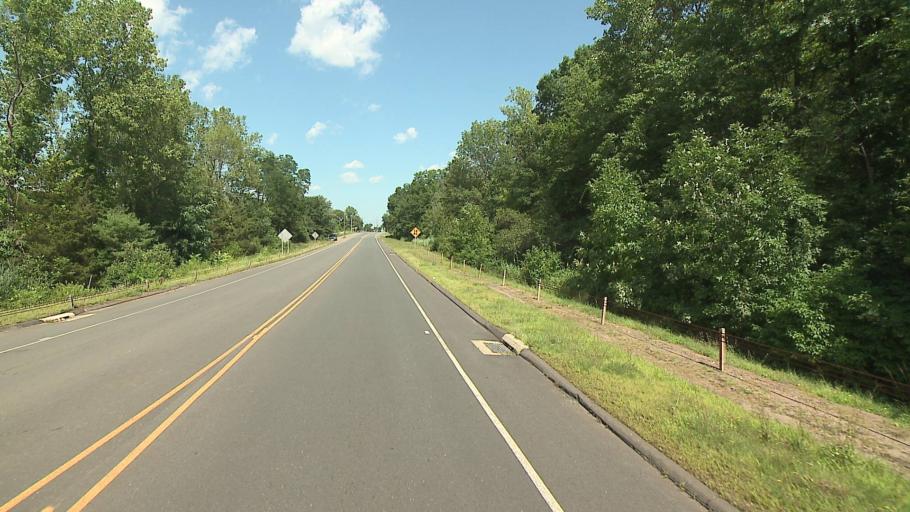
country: US
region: Connecticut
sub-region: Hartford County
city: Farmington
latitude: 41.7208
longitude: -72.7916
